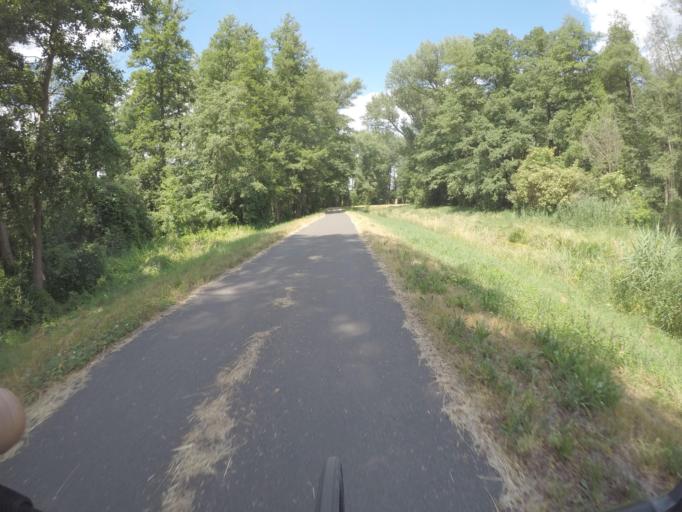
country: DE
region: Brandenburg
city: Brandenburg an der Havel
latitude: 52.4279
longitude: 12.6450
